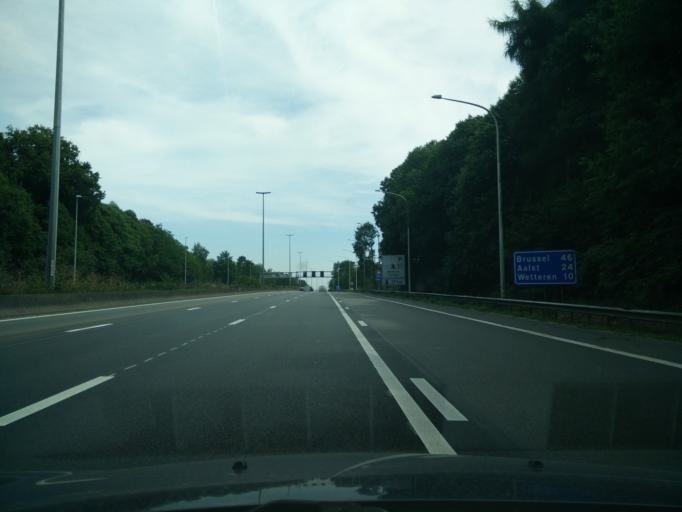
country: BE
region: Flanders
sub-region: Provincie Oost-Vlaanderen
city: Melle
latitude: 50.9975
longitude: 3.7764
